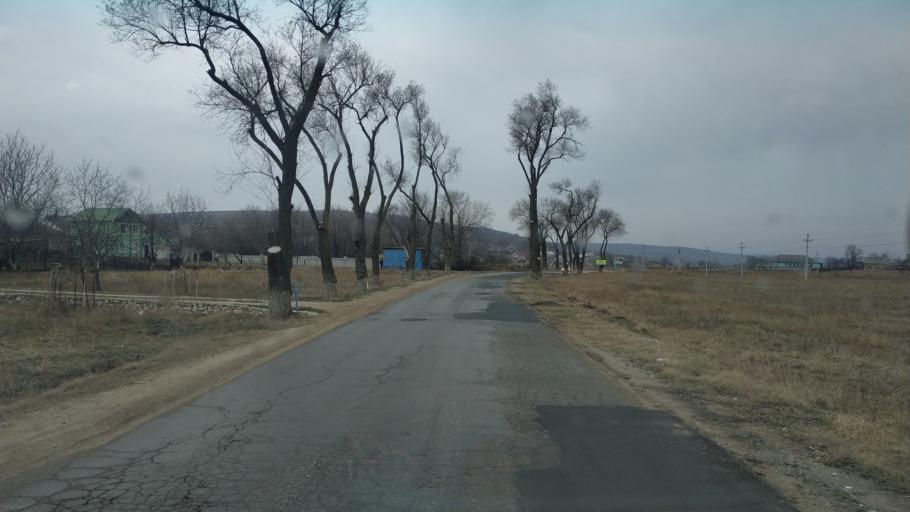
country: MD
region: Chisinau
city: Singera
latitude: 46.9064
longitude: 28.9539
